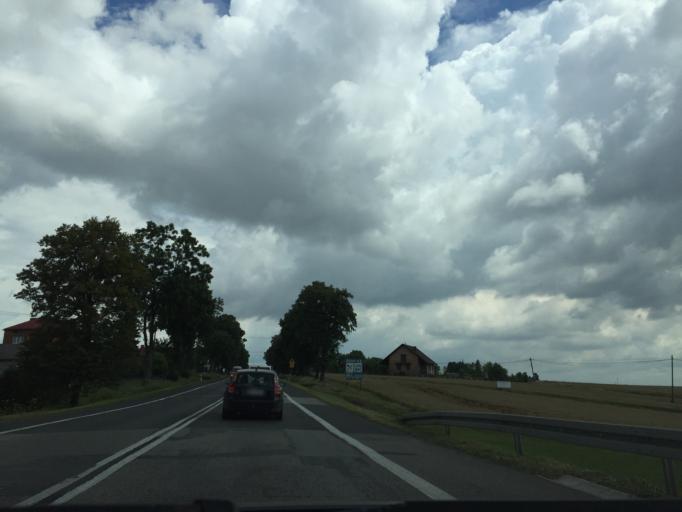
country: PL
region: Lesser Poland Voivodeship
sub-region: Powiat krakowski
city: Slomniki
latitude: 50.2283
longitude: 20.0555
